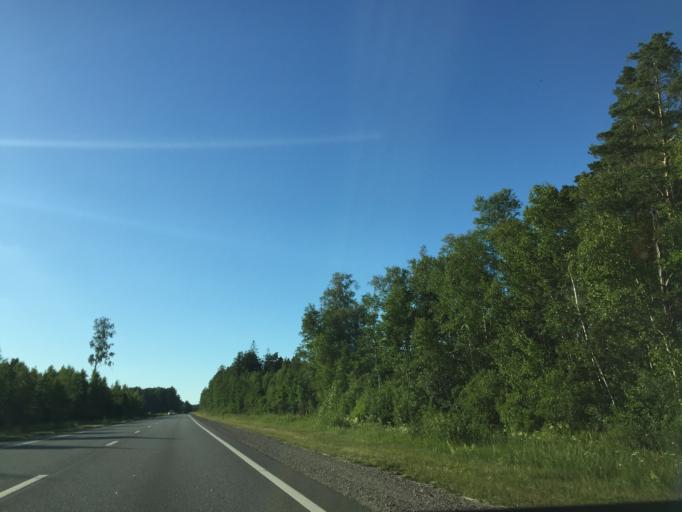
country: LV
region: Ventspils
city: Ventspils
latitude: 57.3827
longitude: 21.7105
